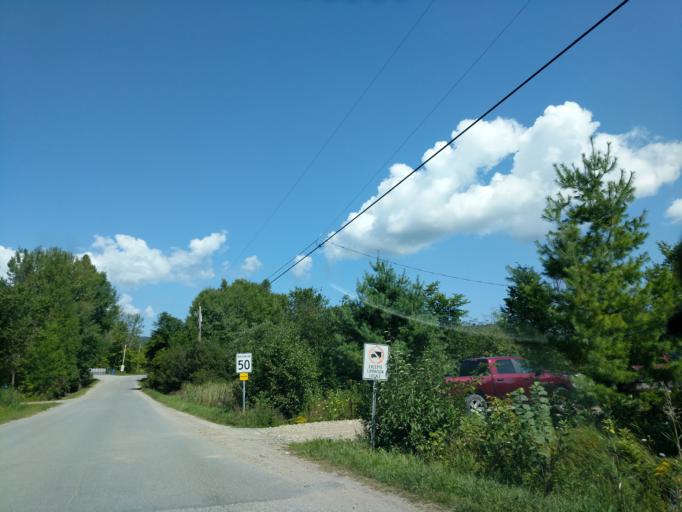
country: CA
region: Quebec
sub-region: Outaouais
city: Wakefield
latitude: 45.5032
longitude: -75.9531
